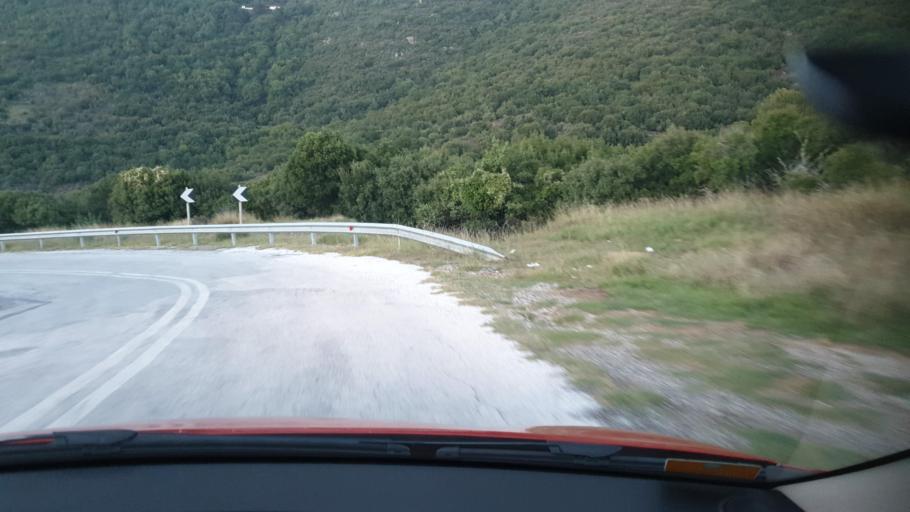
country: GR
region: Central Macedonia
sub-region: Nomos Thessalonikis
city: Peristera
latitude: 40.5235
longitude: 23.2019
